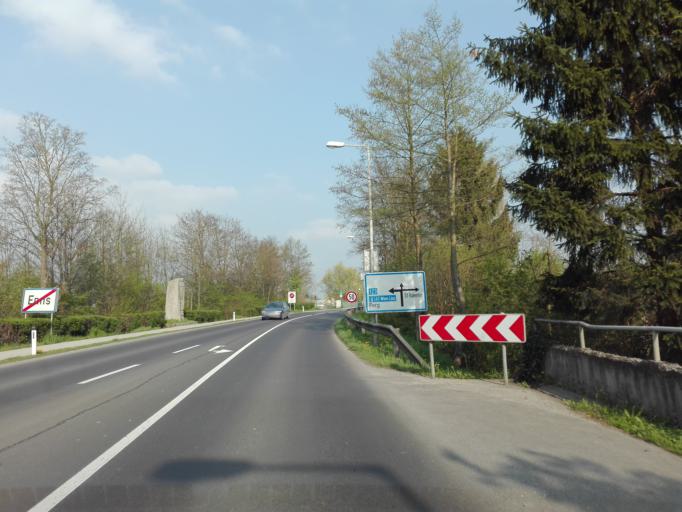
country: AT
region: Upper Austria
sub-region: Politischer Bezirk Linz-Land
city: Enns
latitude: 48.2131
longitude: 14.4838
